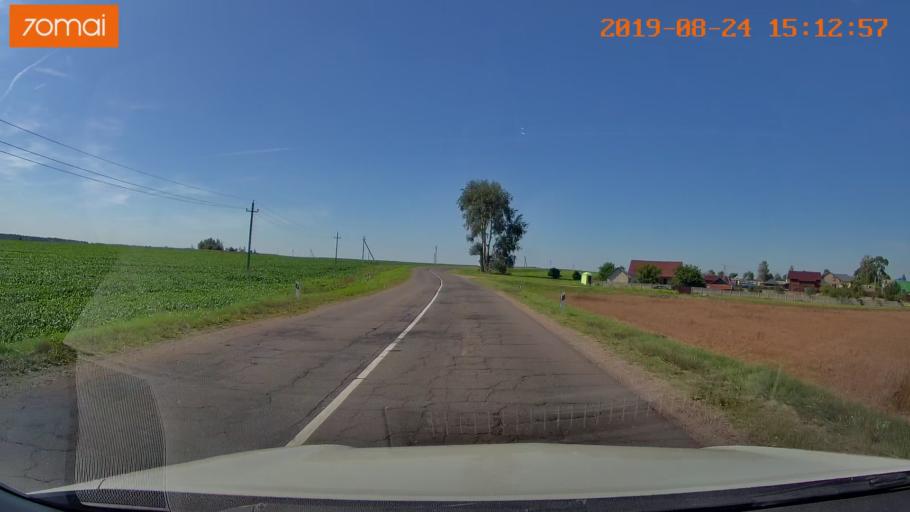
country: BY
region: Minsk
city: Samakhvalavichy
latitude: 53.6065
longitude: 27.5787
